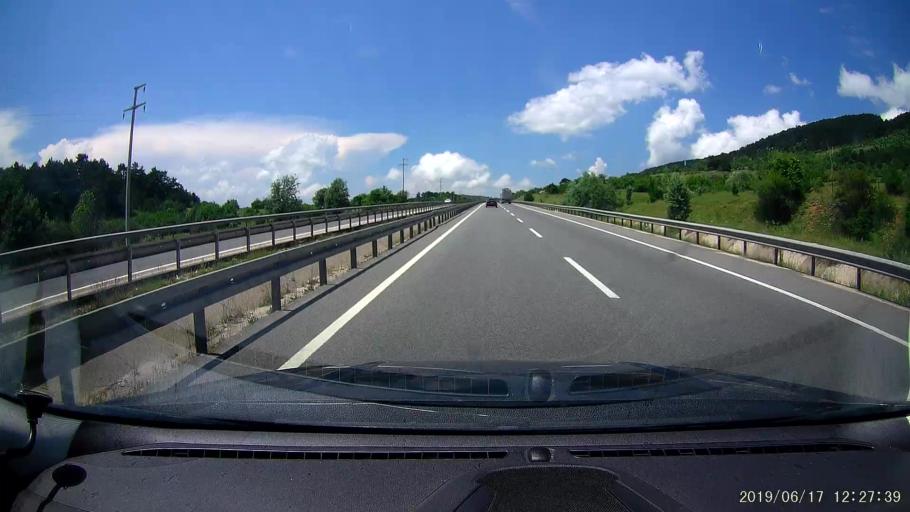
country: TR
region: Bolu
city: Gerede
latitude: 40.8126
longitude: 32.2692
